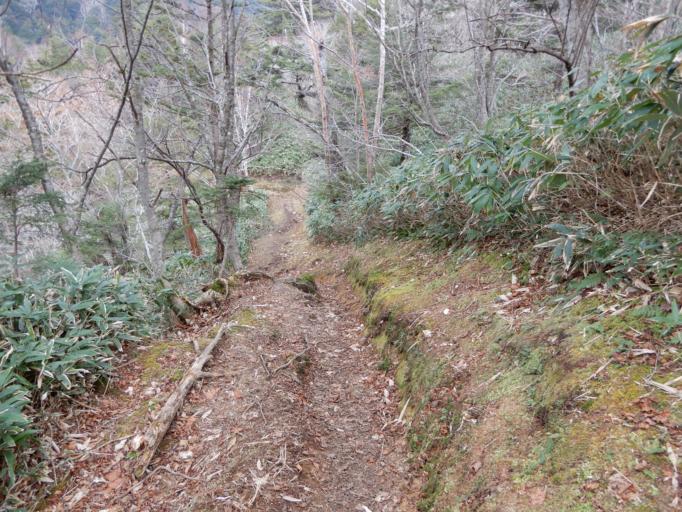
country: JP
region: Gunma
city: Nakanojomachi
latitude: 36.7214
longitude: 138.6460
